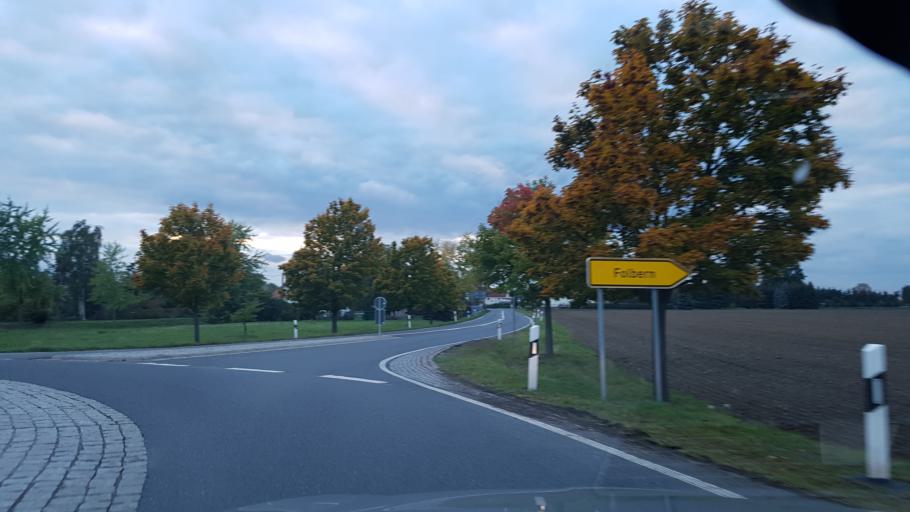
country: DE
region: Saxony
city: Grossenhain
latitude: 51.2999
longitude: 13.5975
